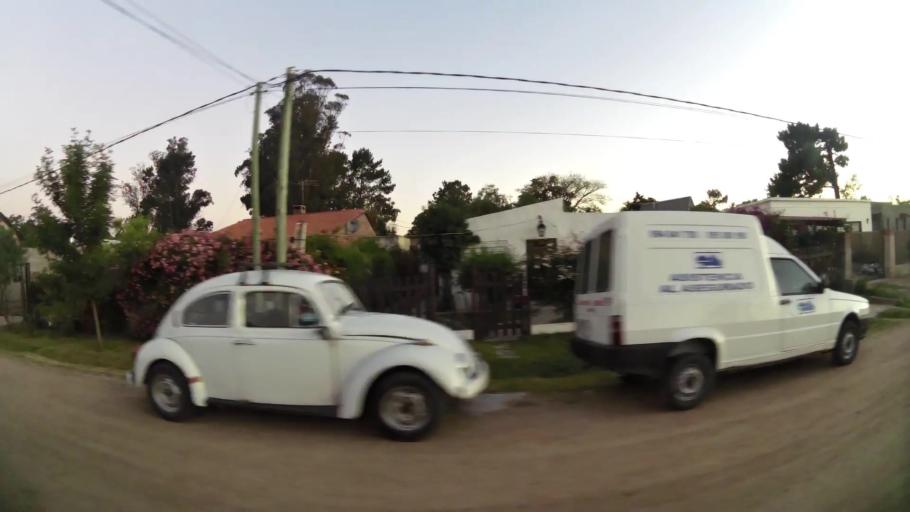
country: UY
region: Canelones
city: Colonia Nicolich
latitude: -34.8181
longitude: -55.9621
